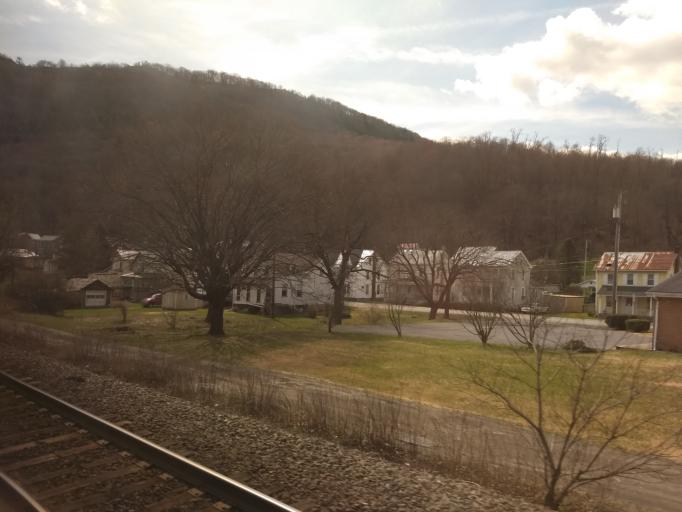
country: US
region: Pennsylvania
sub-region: Huntingdon County
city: Mount Union
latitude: 40.3922
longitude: -77.9383
